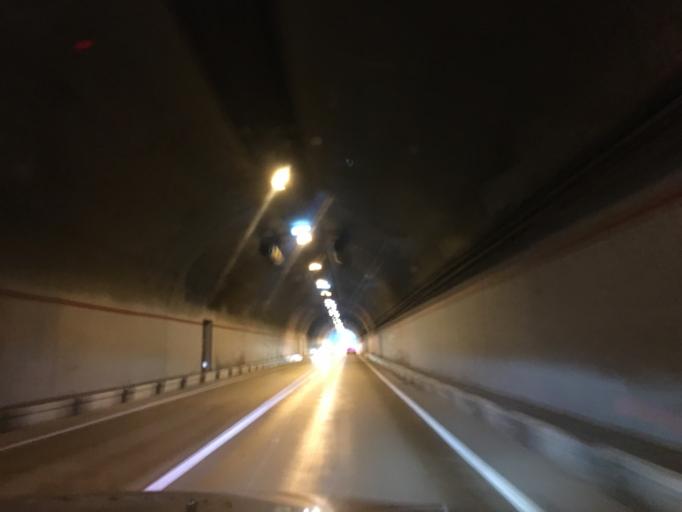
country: RU
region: Krasnodarskiy
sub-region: Sochi City
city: Krasnaya Polyana
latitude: 43.6517
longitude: 40.1509
